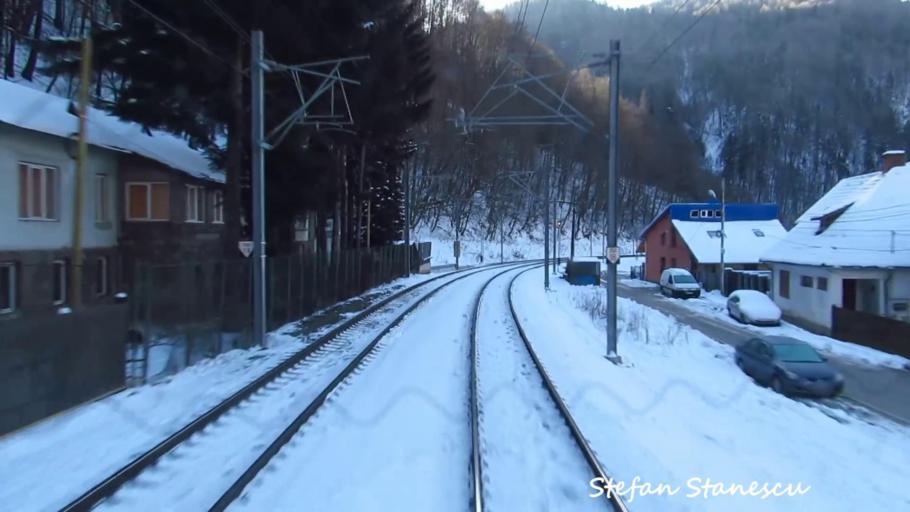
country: RO
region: Prahova
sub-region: Oras Sinaia
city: Sinaia
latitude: 45.3654
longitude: 25.5491
